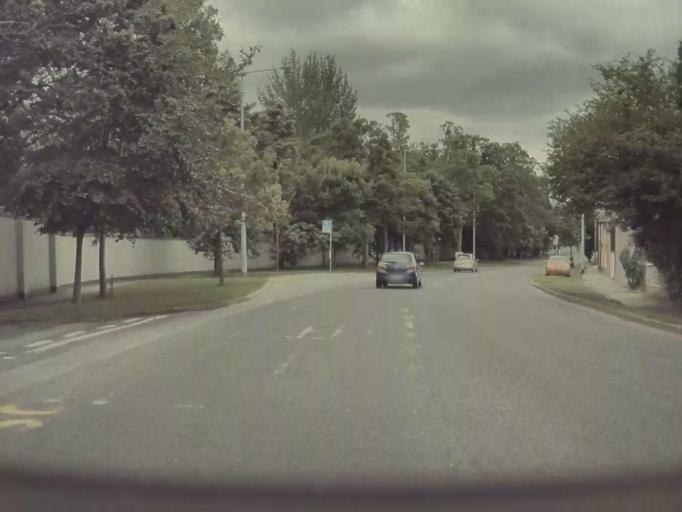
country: IE
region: Leinster
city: Mount Merrion
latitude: 53.2936
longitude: -6.2231
